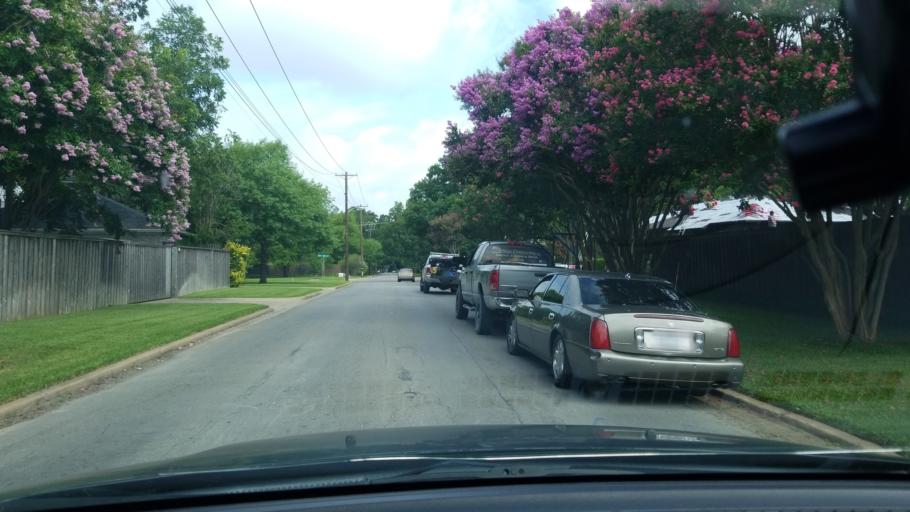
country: US
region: Texas
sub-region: Dallas County
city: Highland Park
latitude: 32.8160
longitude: -96.7144
